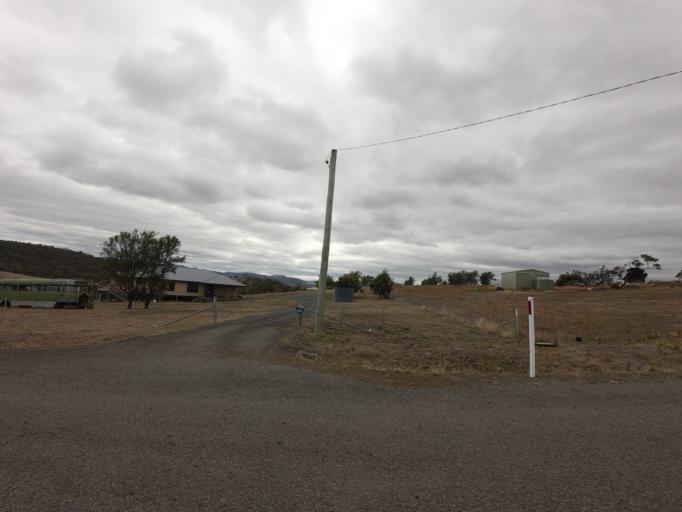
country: AU
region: Tasmania
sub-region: Clarence
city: Warrane
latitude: -42.7934
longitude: 147.3957
